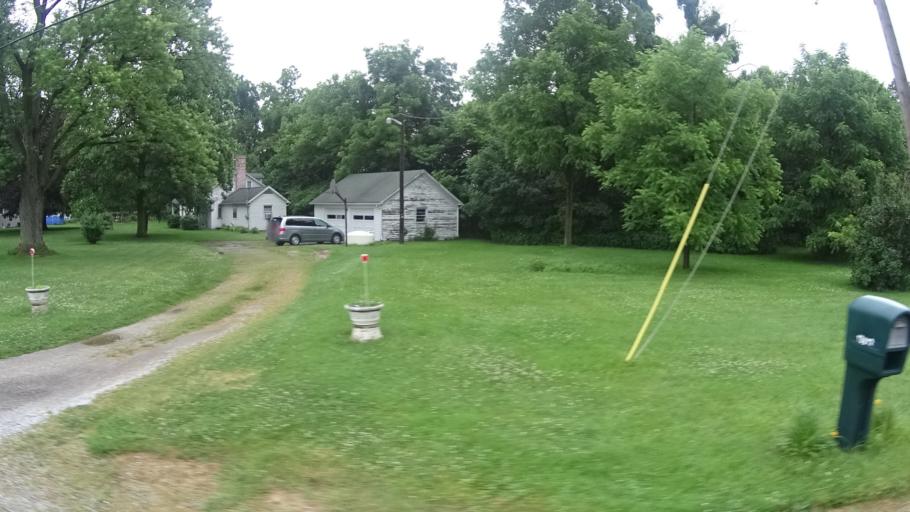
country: US
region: Ohio
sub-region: Erie County
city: Milan
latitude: 41.3100
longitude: -82.6048
